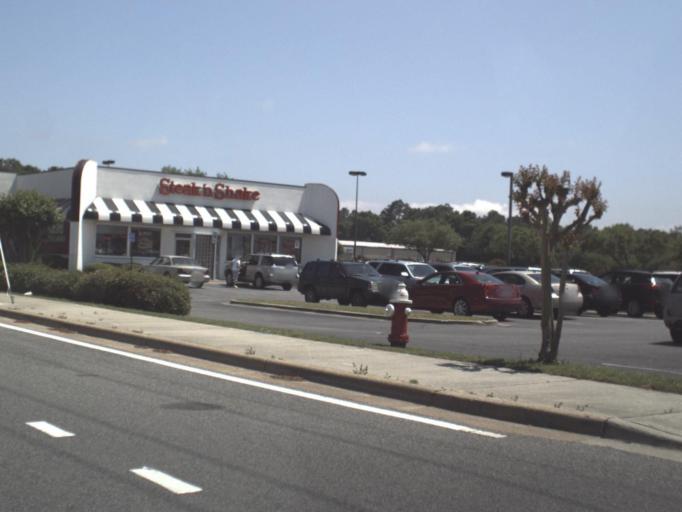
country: US
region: Florida
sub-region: Escambia County
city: Brent
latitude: 30.4775
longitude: -87.2053
